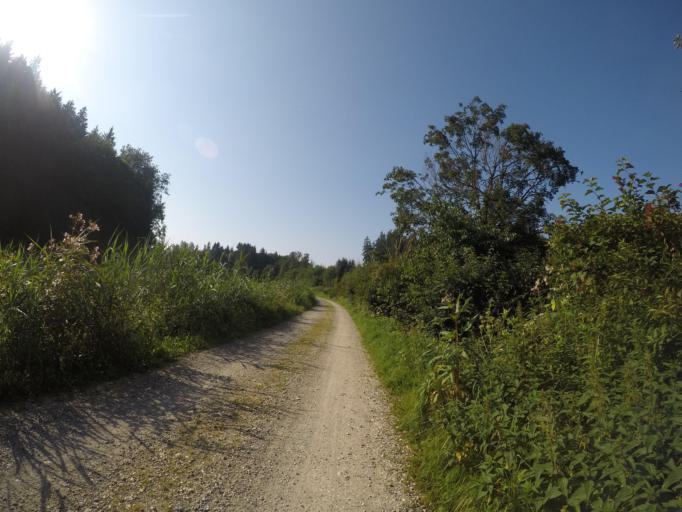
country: DE
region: Baden-Wuerttemberg
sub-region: Tuebingen Region
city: Schnurpflingen
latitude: 48.2535
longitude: 10.0069
